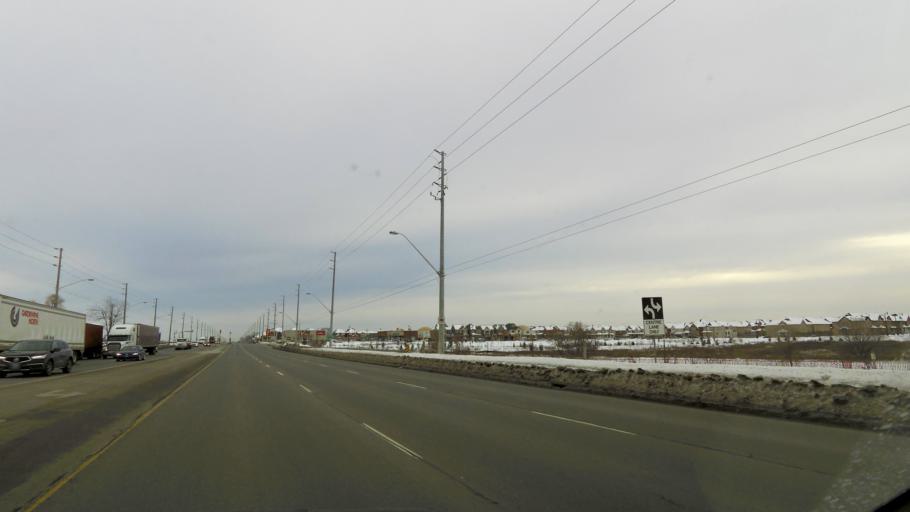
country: CA
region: Ontario
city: Brampton
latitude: 43.7996
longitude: -79.6672
